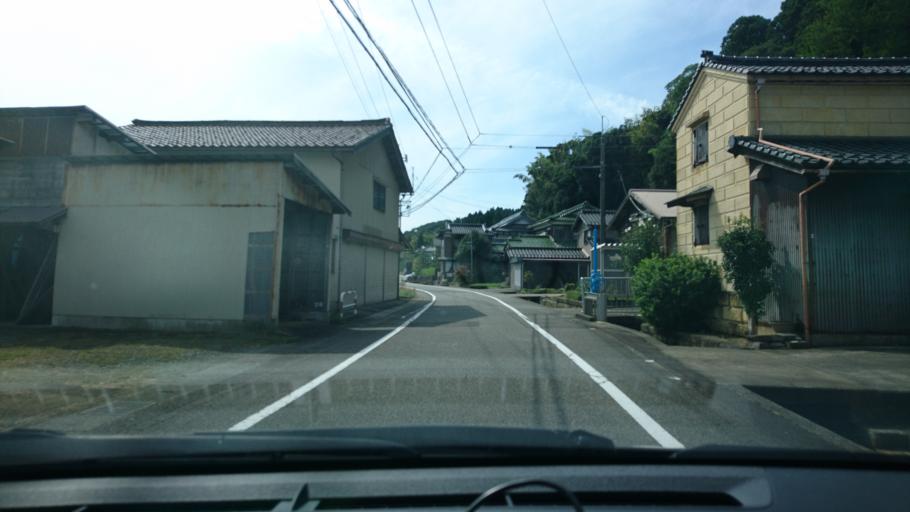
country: JP
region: Fukui
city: Maruoka
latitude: 36.2874
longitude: 136.2947
